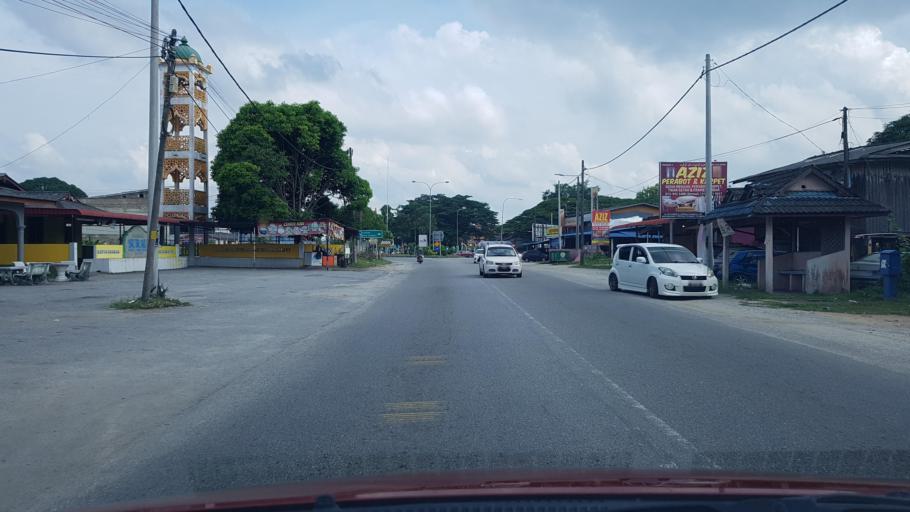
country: MY
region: Terengganu
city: Kuala Terengganu
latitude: 5.3489
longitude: 103.0927
